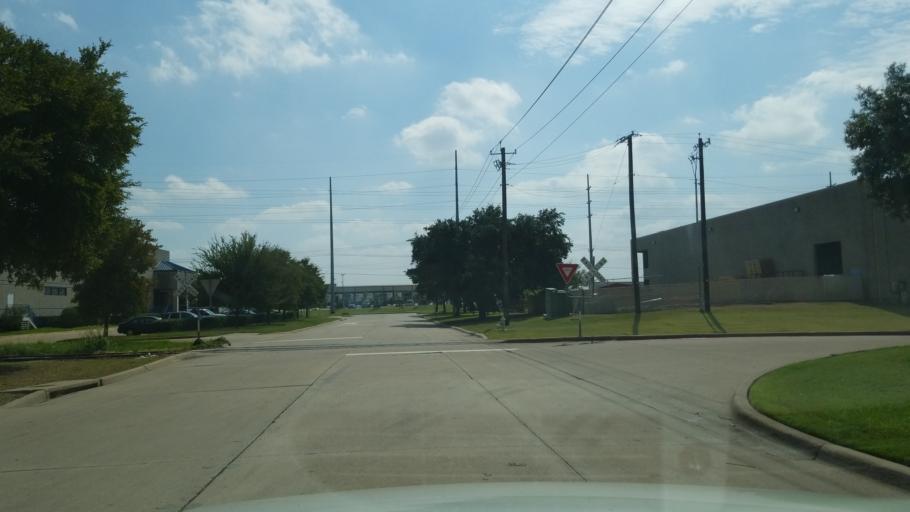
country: US
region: Texas
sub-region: Dallas County
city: Garland
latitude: 32.9024
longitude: -96.6711
